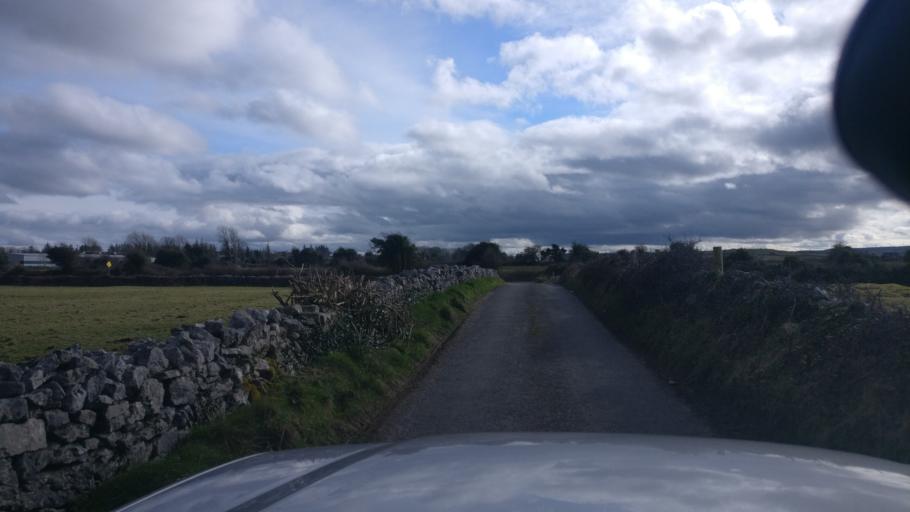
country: IE
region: Connaught
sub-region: County Galway
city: Loughrea
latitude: 53.1975
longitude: -8.5420
